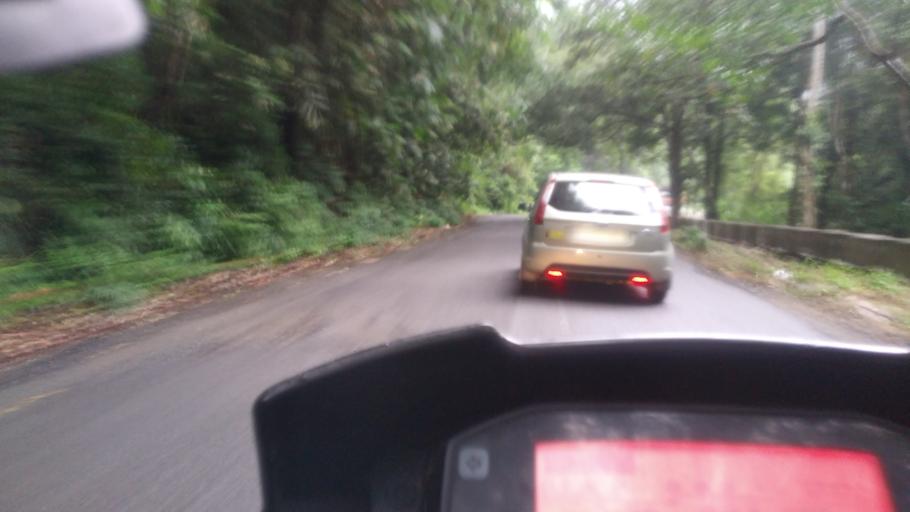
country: IN
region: Kerala
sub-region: Idukki
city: Kuttampuzha
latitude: 10.0644
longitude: 76.7976
